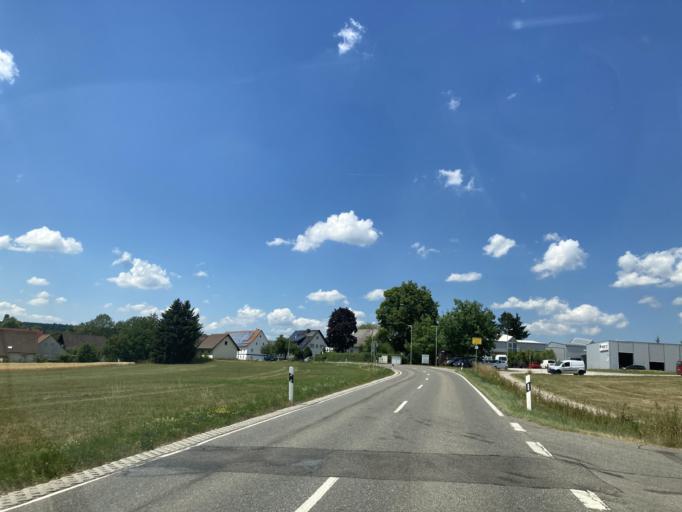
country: DE
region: Baden-Wuerttemberg
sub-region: Freiburg Region
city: Monchweiler
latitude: 48.0338
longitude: 8.4275
